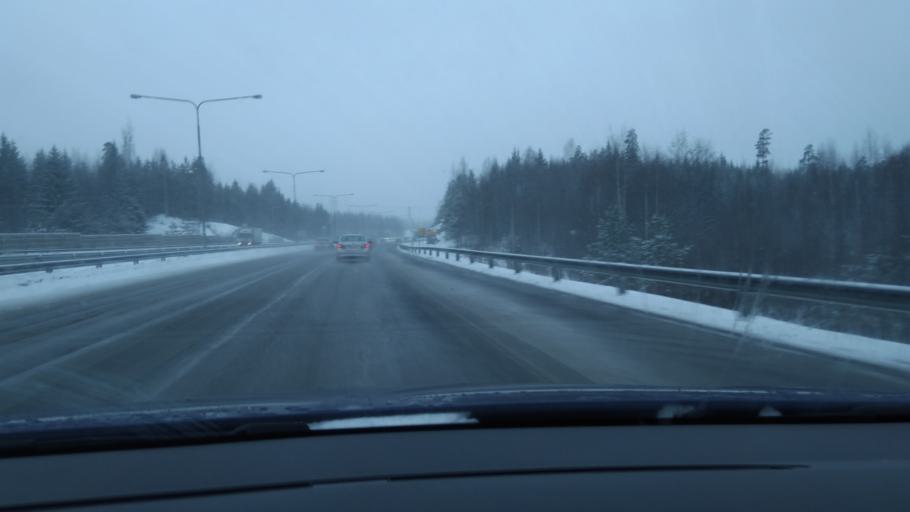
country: FI
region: Pirkanmaa
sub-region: Tampere
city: Tampere
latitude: 61.5026
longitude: 23.8940
